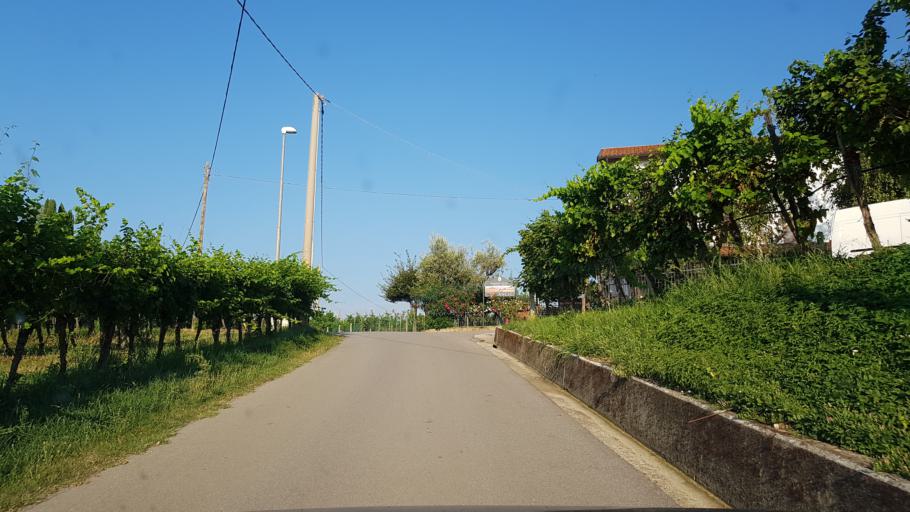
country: IT
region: Friuli Venezia Giulia
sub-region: Provincia di Gorizia
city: Cormons
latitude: 45.9522
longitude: 13.4870
